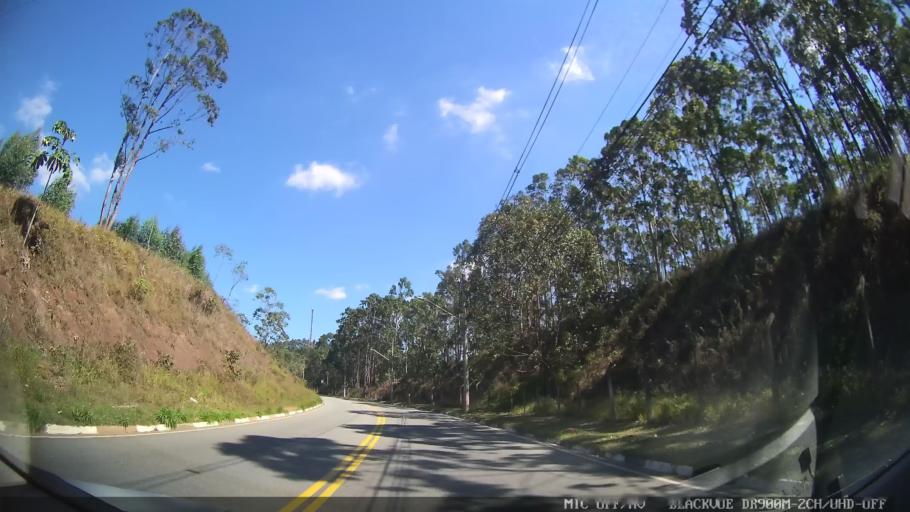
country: BR
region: Sao Paulo
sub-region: Barueri
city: Barueri
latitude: -23.4506
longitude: -46.8382
